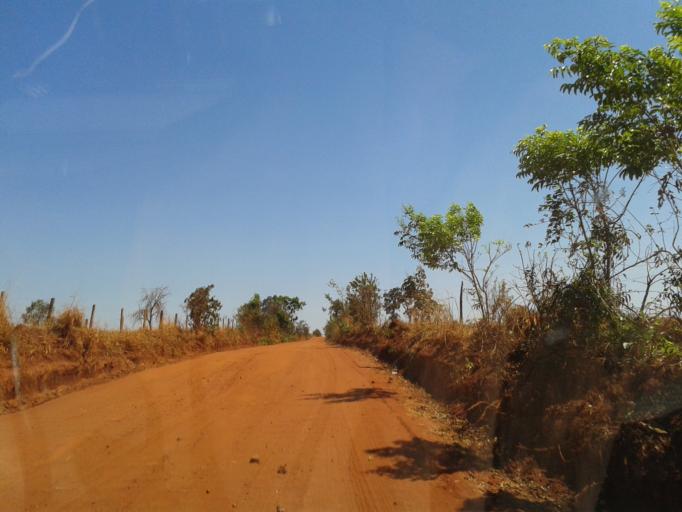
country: BR
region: Minas Gerais
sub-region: Ituiutaba
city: Ituiutaba
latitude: -18.9859
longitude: -49.3913
